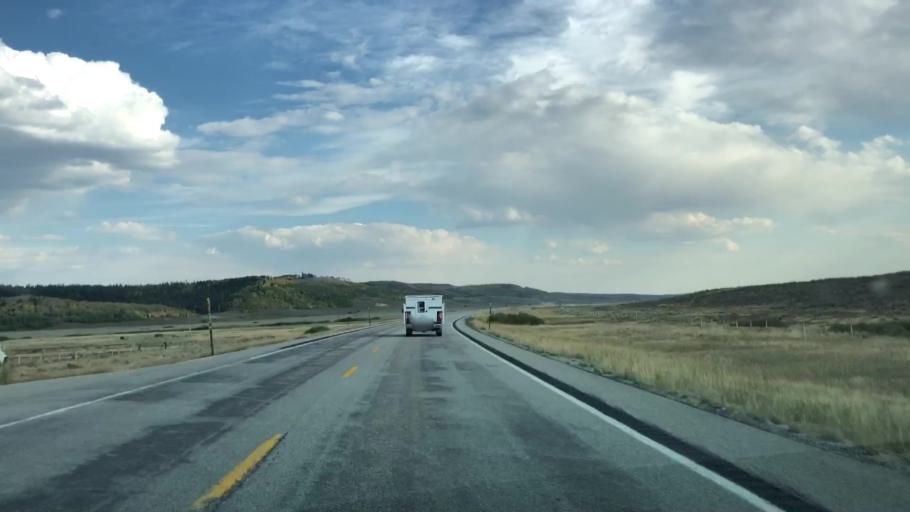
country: US
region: Wyoming
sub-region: Sublette County
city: Pinedale
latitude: 43.1153
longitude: -110.1759
